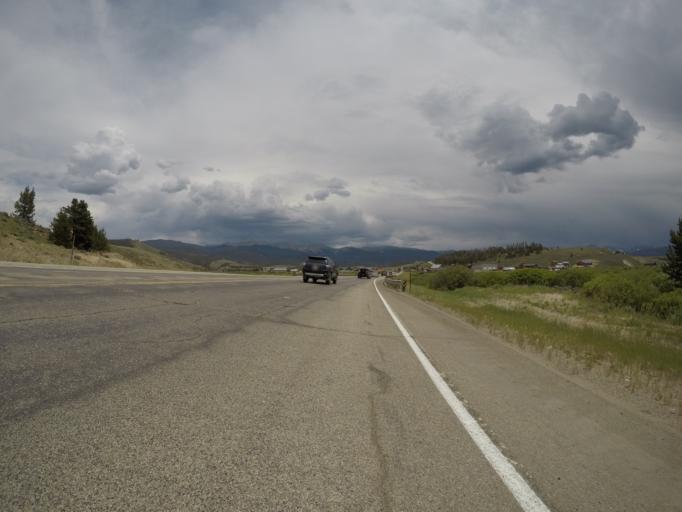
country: US
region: Colorado
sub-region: Grand County
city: Fraser
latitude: 39.9945
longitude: -105.8517
